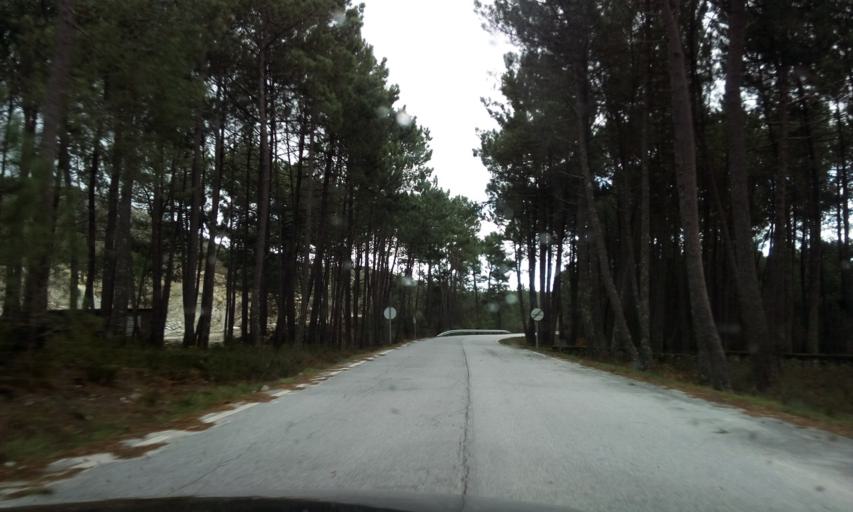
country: PT
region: Guarda
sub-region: Fornos de Algodres
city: Fornos de Algodres
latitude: 40.6325
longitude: -7.6100
